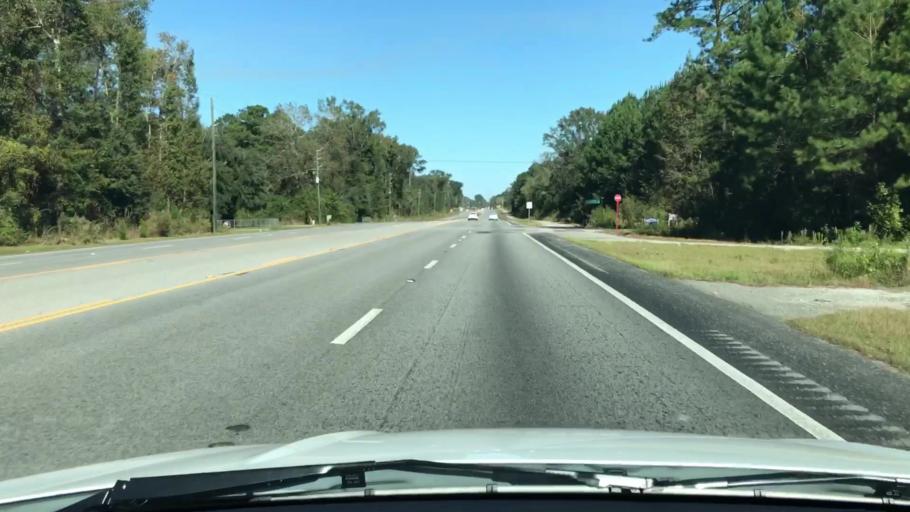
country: US
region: South Carolina
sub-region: Hampton County
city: Yemassee
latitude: 32.6151
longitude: -80.7426
